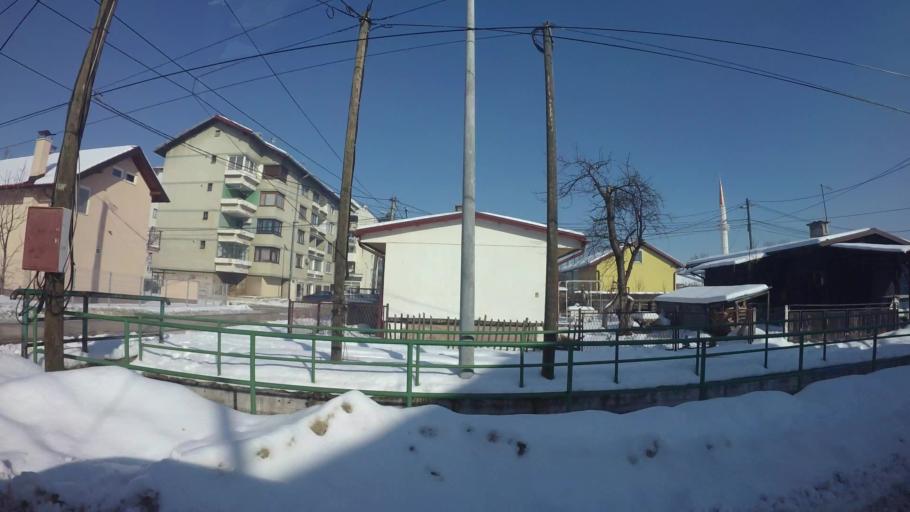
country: BA
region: Federation of Bosnia and Herzegovina
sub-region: Kanton Sarajevo
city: Sarajevo
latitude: 43.7949
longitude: 18.3175
